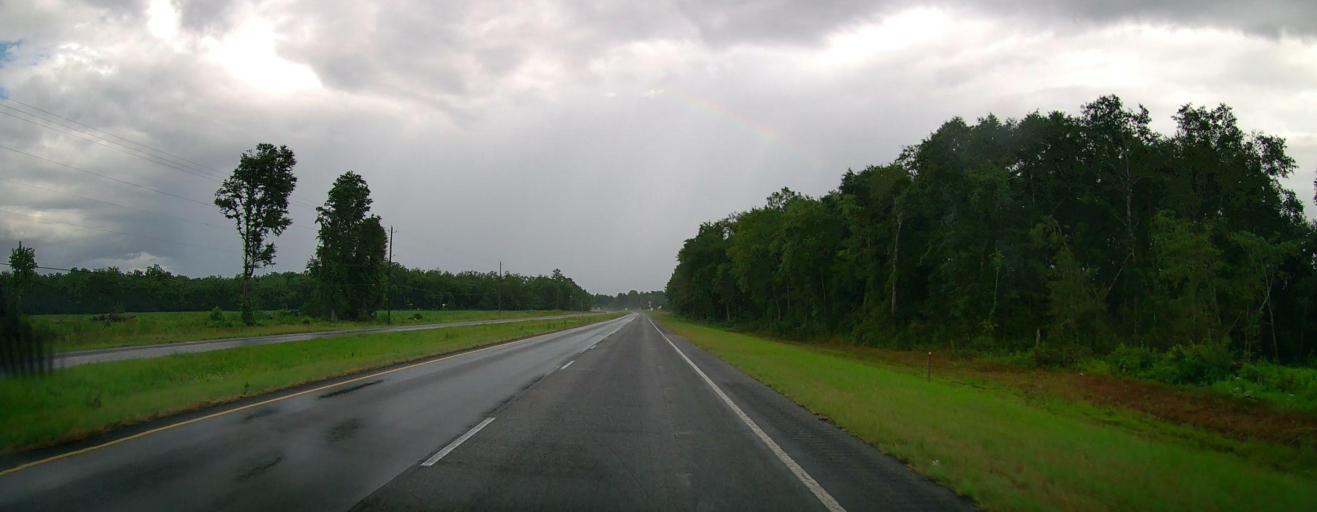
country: US
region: Georgia
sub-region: Ware County
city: Deenwood
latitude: 31.2557
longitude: -82.4877
